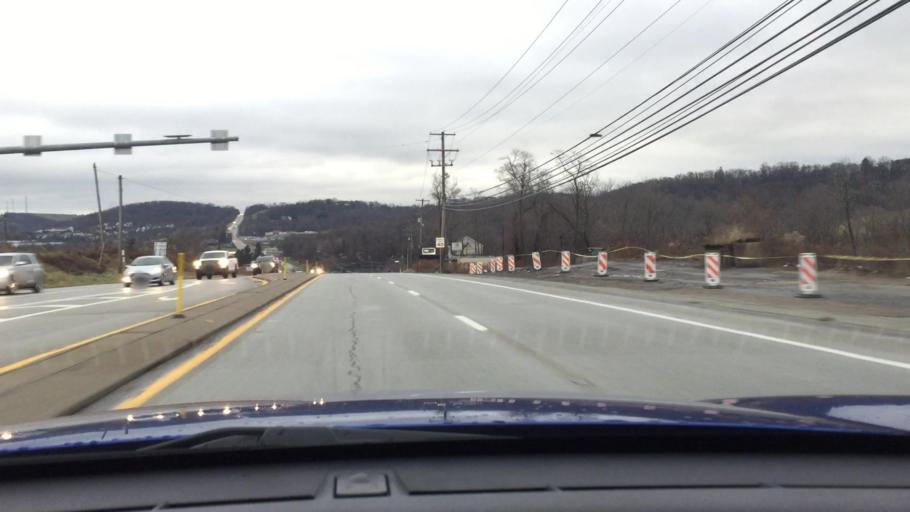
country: US
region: Pennsylvania
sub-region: Washington County
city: McGovern
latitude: 40.2019
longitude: -80.2049
